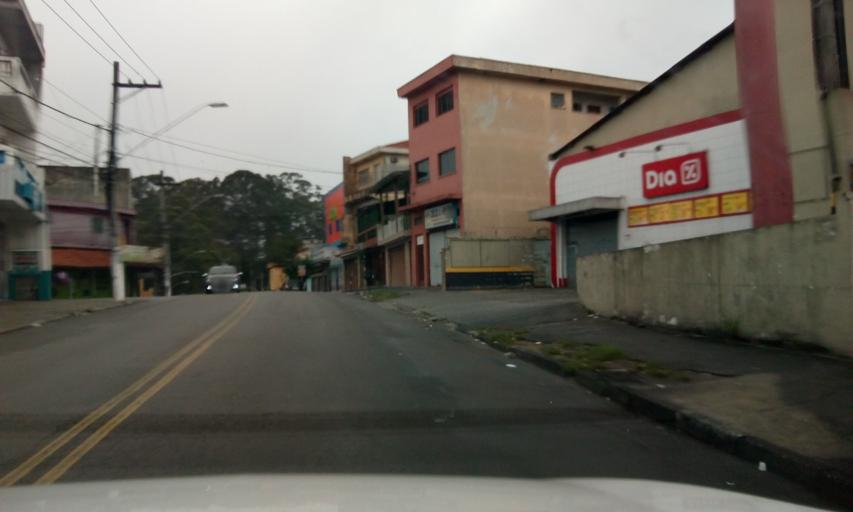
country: BR
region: Sao Paulo
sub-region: Diadema
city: Diadema
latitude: -23.6960
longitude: -46.6274
